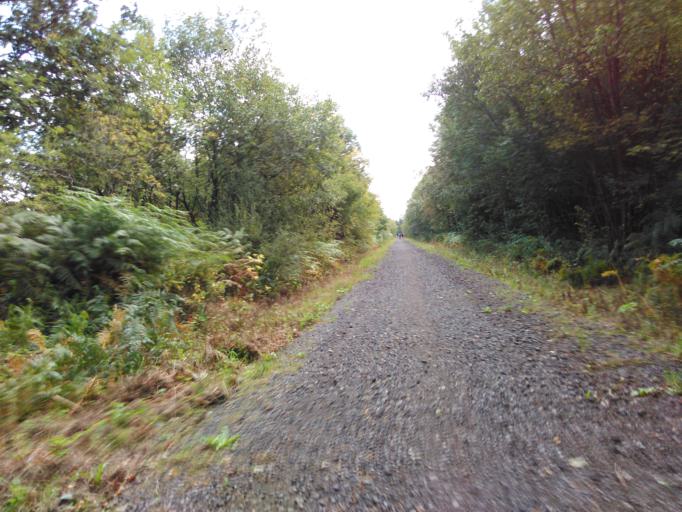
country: BE
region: Wallonia
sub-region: Province du Luxembourg
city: Neufchateau
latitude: 49.9065
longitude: 5.4682
